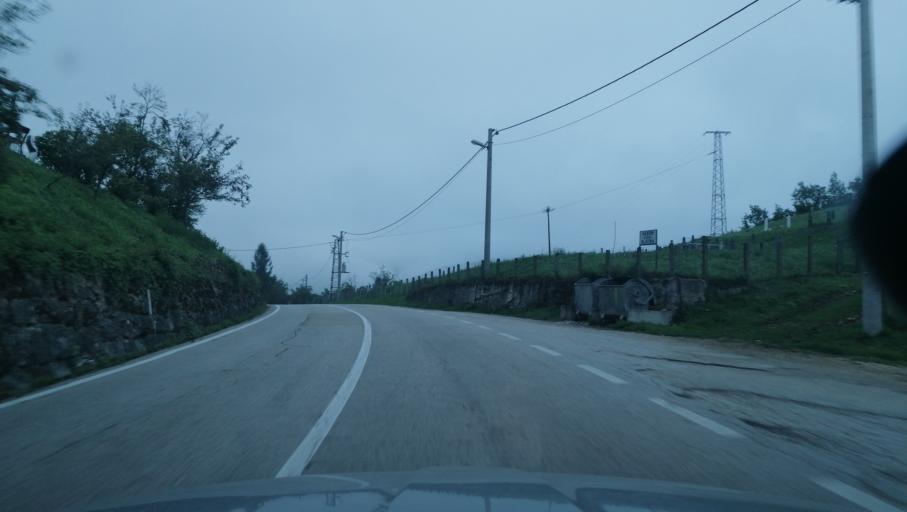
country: BA
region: Federation of Bosnia and Herzegovina
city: Jablanica
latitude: 43.7078
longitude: 17.7176
